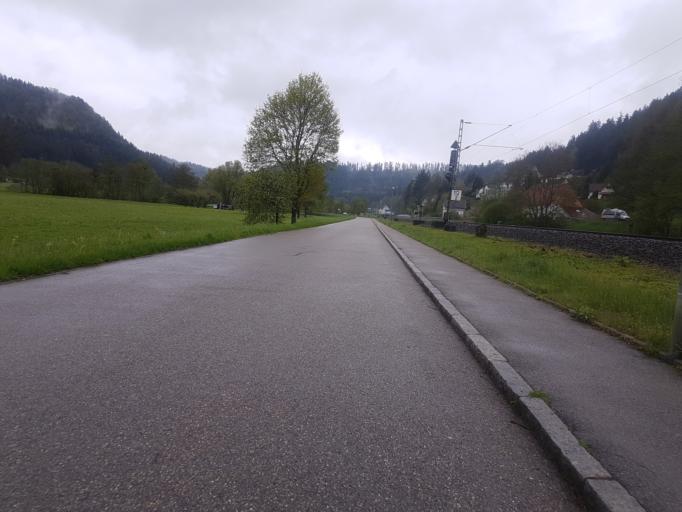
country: DE
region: Baden-Wuerttemberg
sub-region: Freiburg Region
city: Epfendorf
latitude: 48.2448
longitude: 8.5995
